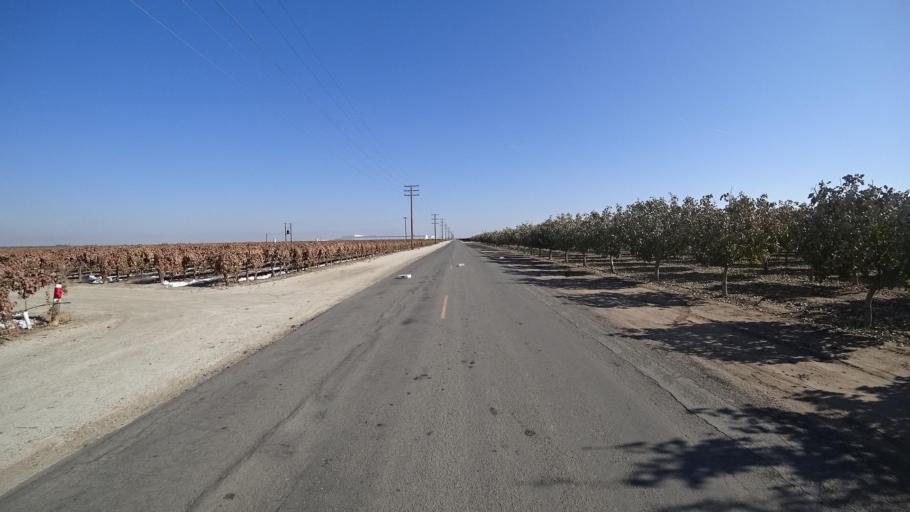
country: US
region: California
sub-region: Kern County
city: McFarland
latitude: 35.7034
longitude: -119.2161
